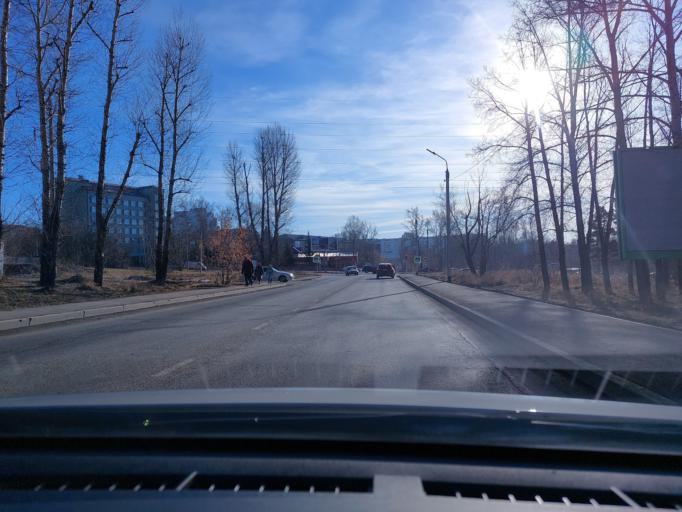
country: RU
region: Irkutsk
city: Dzerzhinsk
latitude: 52.2544
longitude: 104.3519
